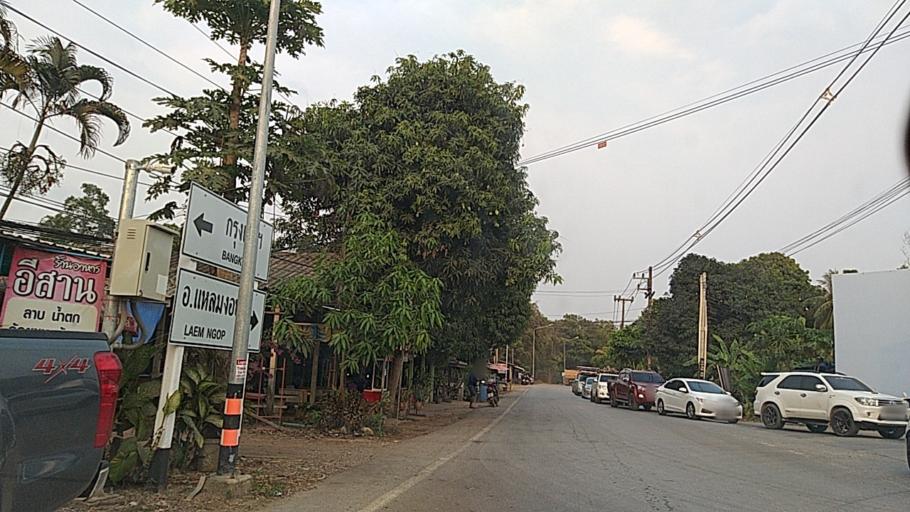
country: TH
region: Trat
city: Laem Ngop
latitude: 12.1894
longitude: 102.3011
